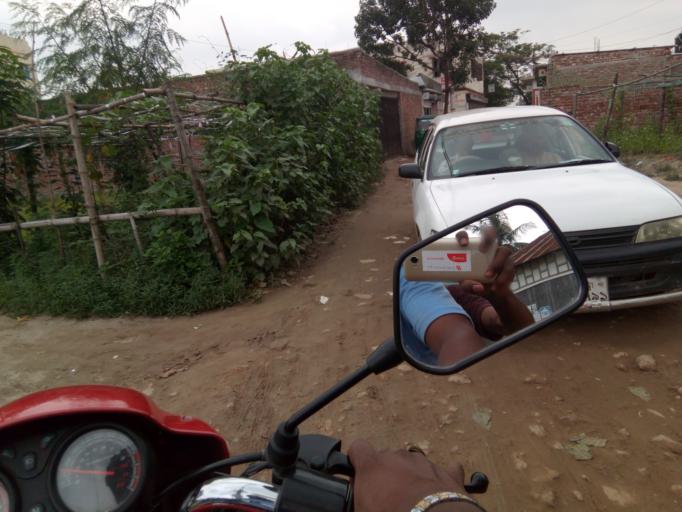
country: BD
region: Dhaka
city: Paltan
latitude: 23.7423
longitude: 90.4613
